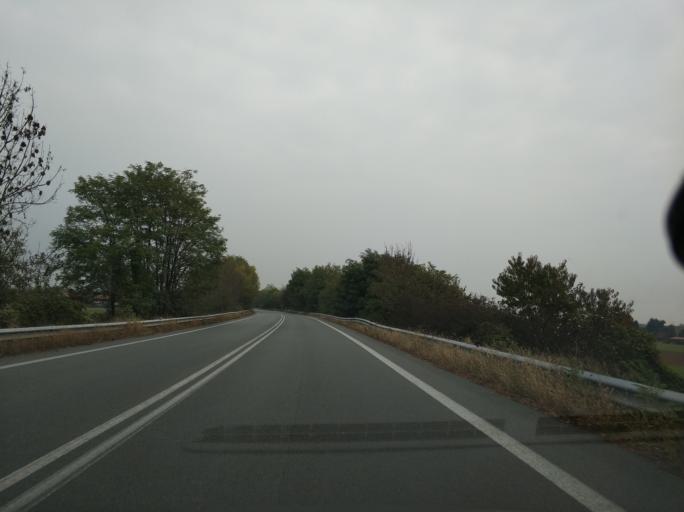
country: IT
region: Piedmont
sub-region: Provincia di Torino
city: Leini
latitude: 45.1981
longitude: 7.7038
